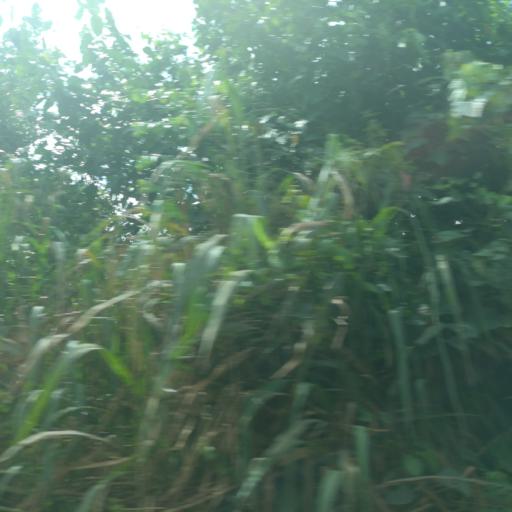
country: NG
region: Lagos
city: Ikorodu
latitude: 6.6712
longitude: 3.6456
